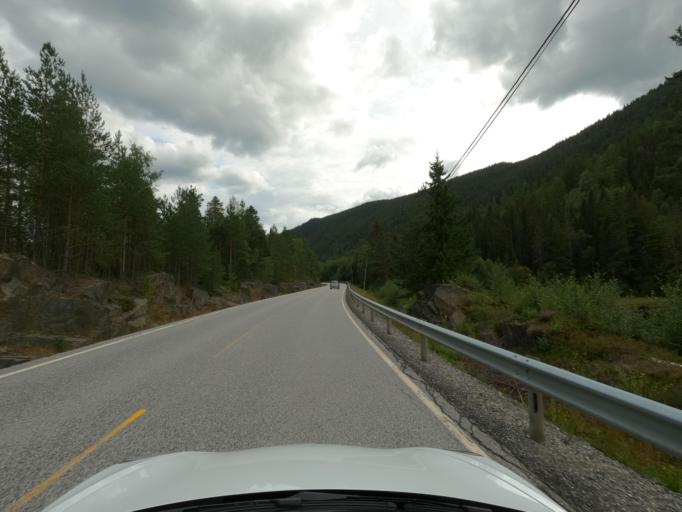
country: NO
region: Telemark
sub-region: Hjartdal
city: Sauland
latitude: 59.8598
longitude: 8.9399
